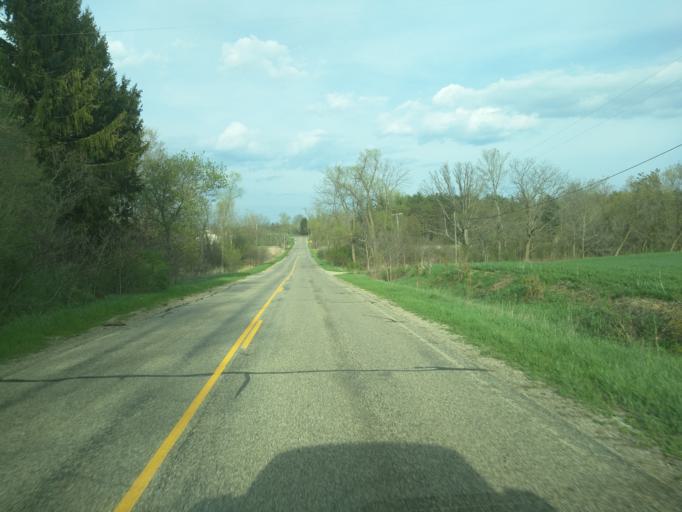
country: US
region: Michigan
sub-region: Eaton County
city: Dimondale
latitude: 42.6257
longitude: -84.6291
